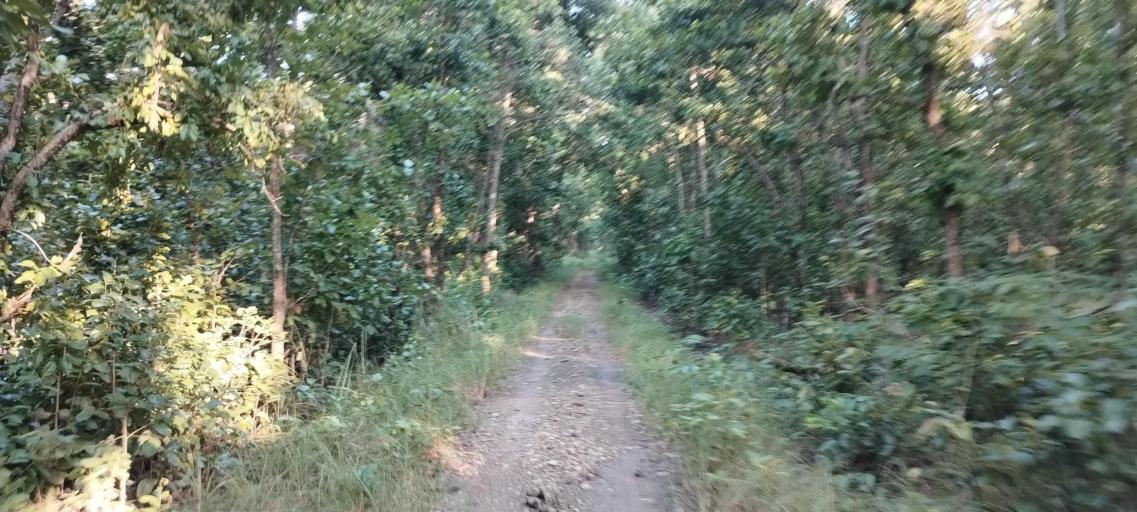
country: NP
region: Far Western
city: Tikapur
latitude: 28.4867
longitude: 81.2620
